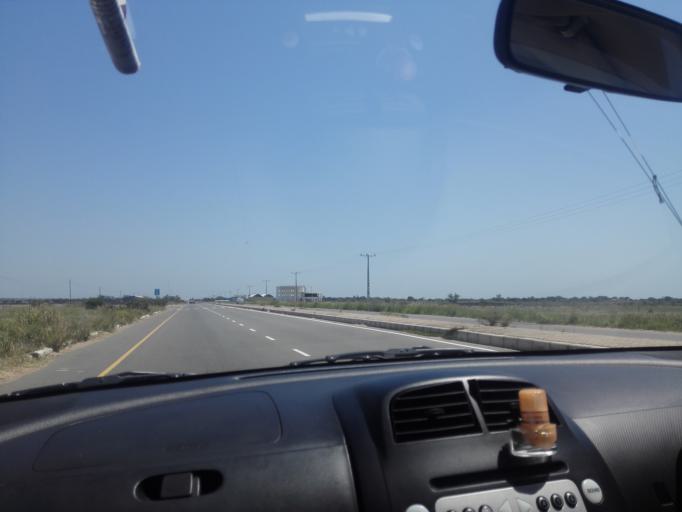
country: MZ
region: Maputo City
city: Maputo
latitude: -25.8256
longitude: 32.6721
